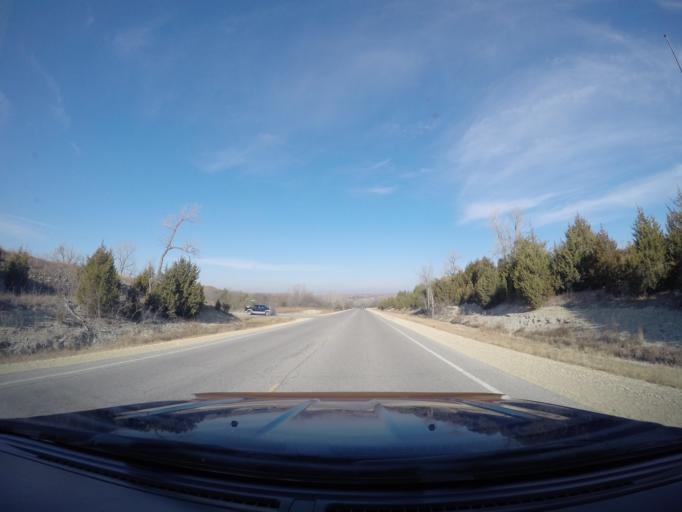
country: US
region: Kansas
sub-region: Riley County
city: Manhattan
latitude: 39.2319
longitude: -96.6202
